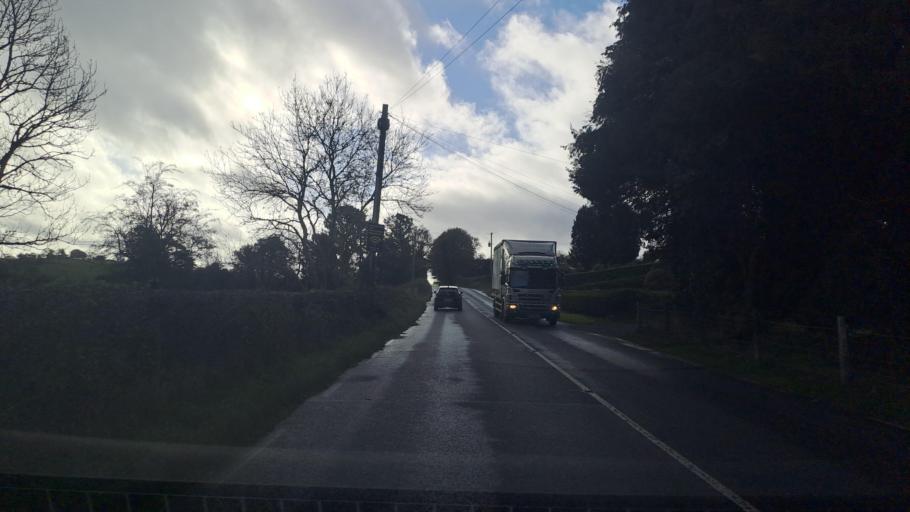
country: IE
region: Ulster
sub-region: County Monaghan
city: Monaghan
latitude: 54.2266
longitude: -6.9717
